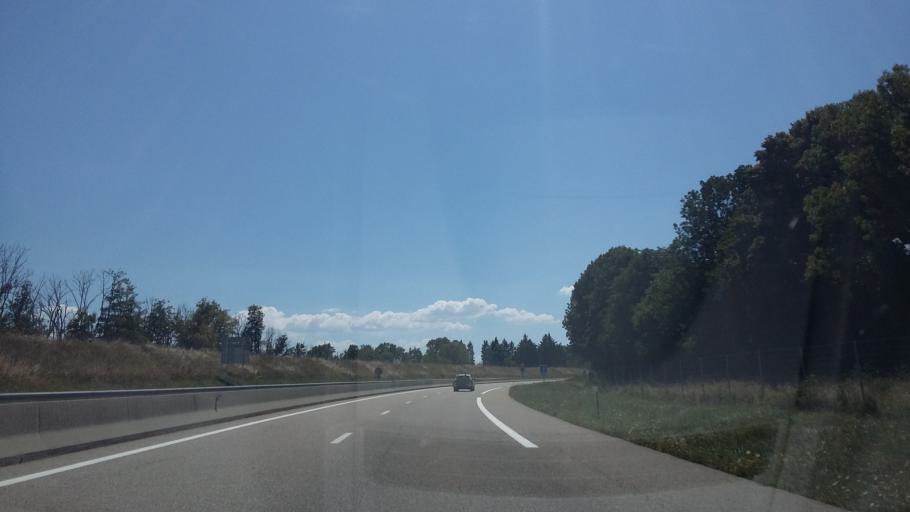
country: FR
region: Rhone-Alpes
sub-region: Departement de l'Isere
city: La Motte-Saint-Martin
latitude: 44.9548
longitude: 5.6558
